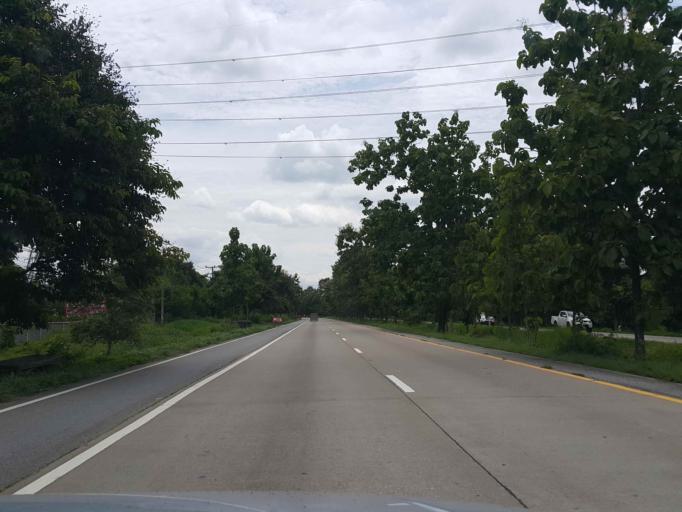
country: TH
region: Lamphun
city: Mae Tha
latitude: 18.4825
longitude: 99.1289
